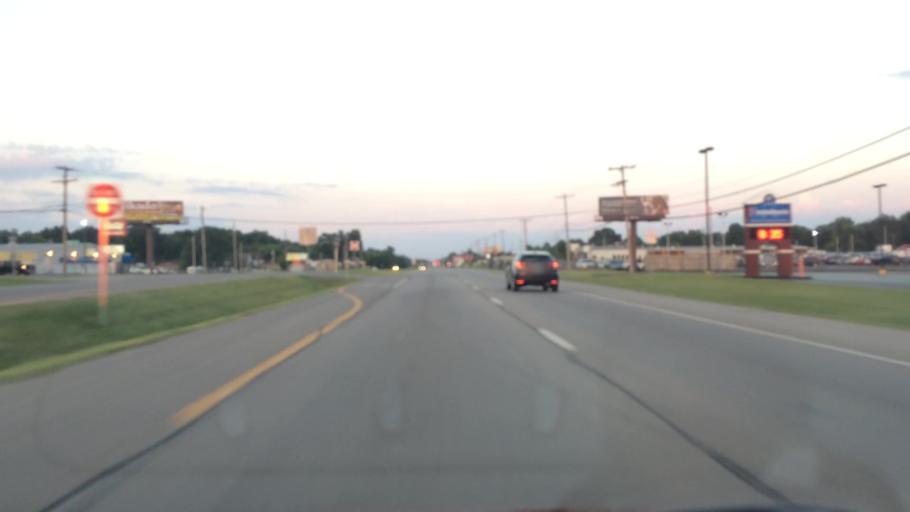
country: US
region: Missouri
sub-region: Greene County
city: Springfield
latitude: 37.1829
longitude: -93.3412
